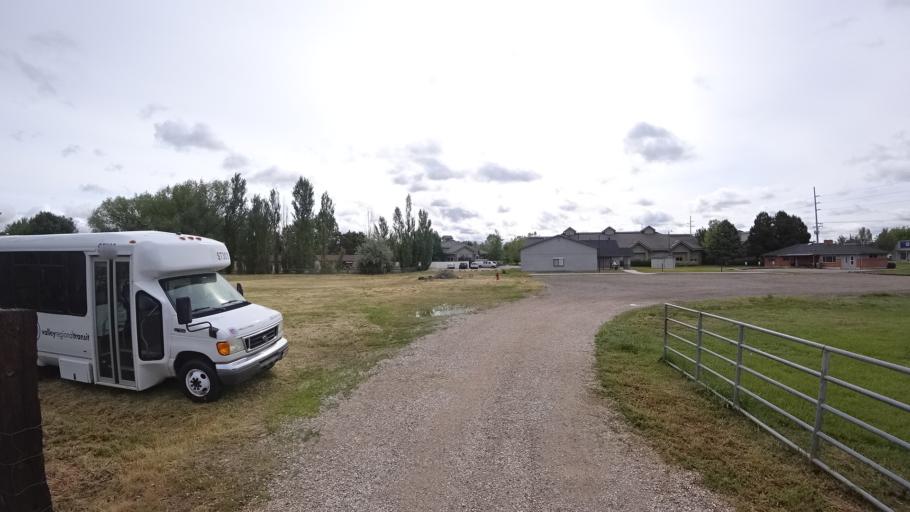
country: US
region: Idaho
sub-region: Ada County
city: Eagle
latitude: 43.6961
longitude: -116.3498
